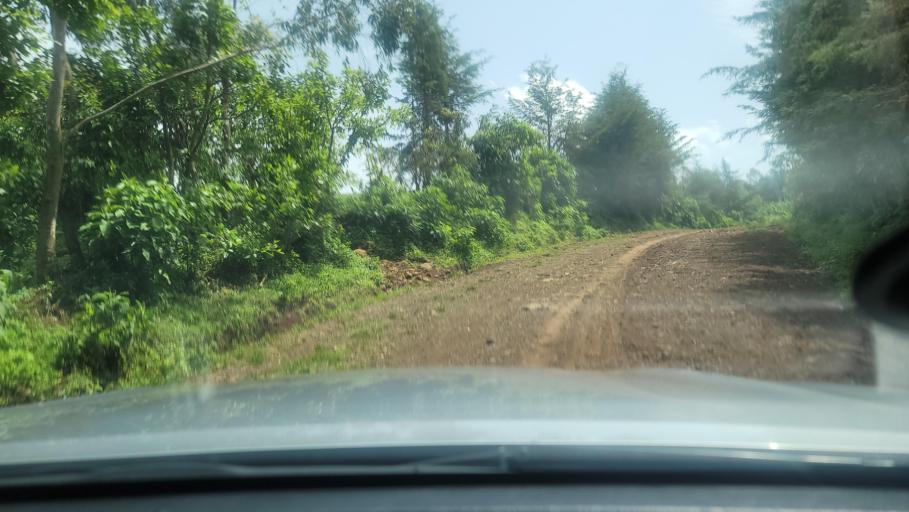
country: ET
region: Oromiya
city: Agaro
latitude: 7.8342
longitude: 36.4051
